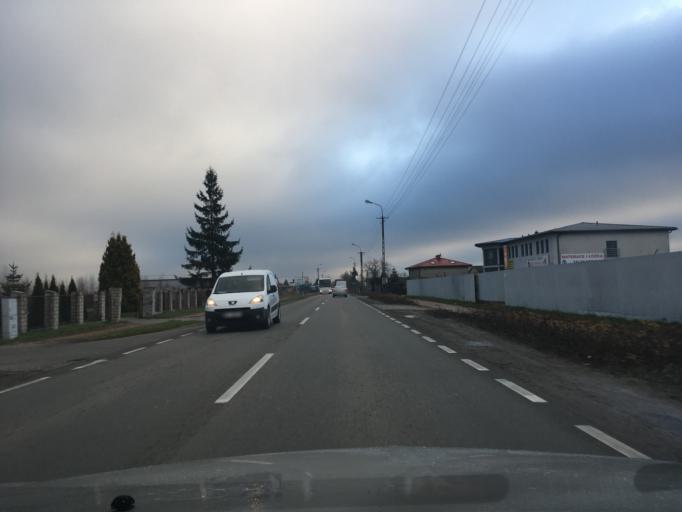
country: PL
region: Masovian Voivodeship
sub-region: Powiat piaseczynski
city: Lesznowola
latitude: 52.0853
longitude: 20.9515
